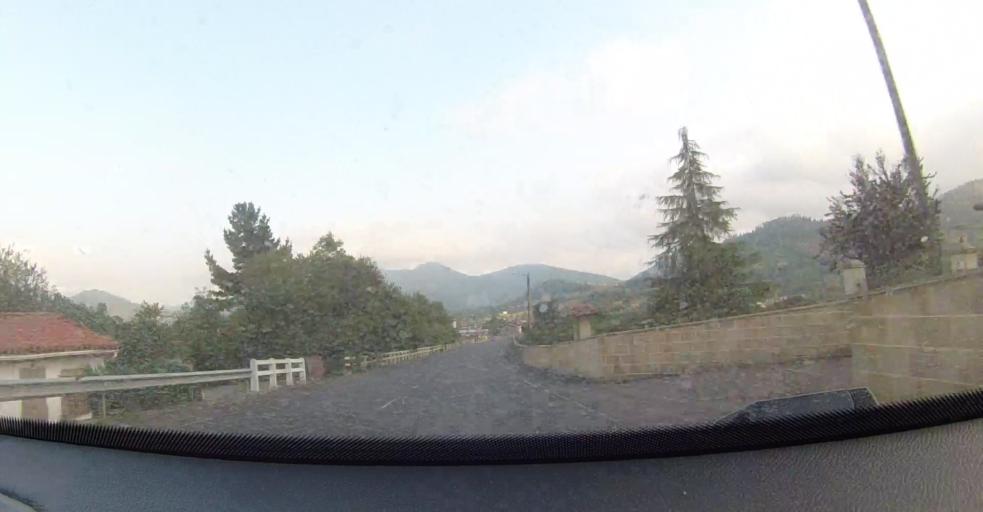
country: ES
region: Basque Country
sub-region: Bizkaia
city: Sopuerta
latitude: 43.2822
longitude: -3.1610
